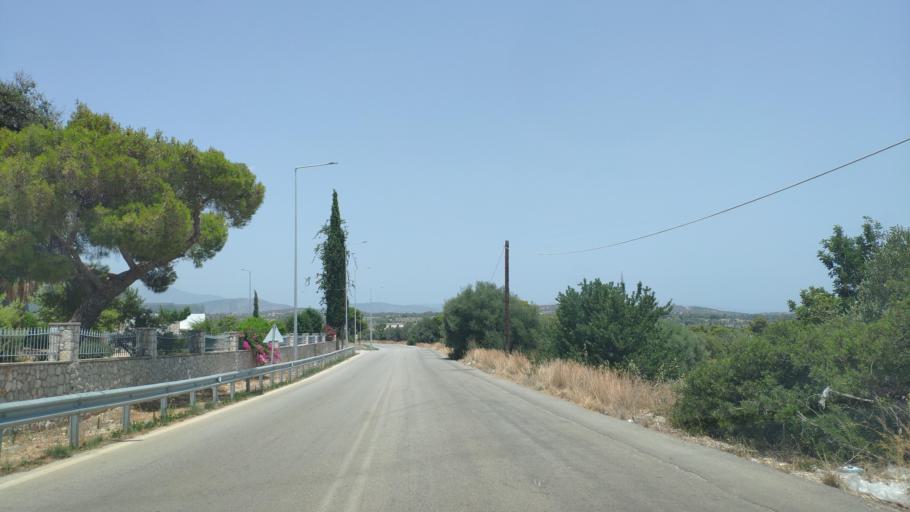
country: GR
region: Peloponnese
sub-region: Nomos Argolidos
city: Porto Cheli
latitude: 37.3368
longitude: 23.1545
